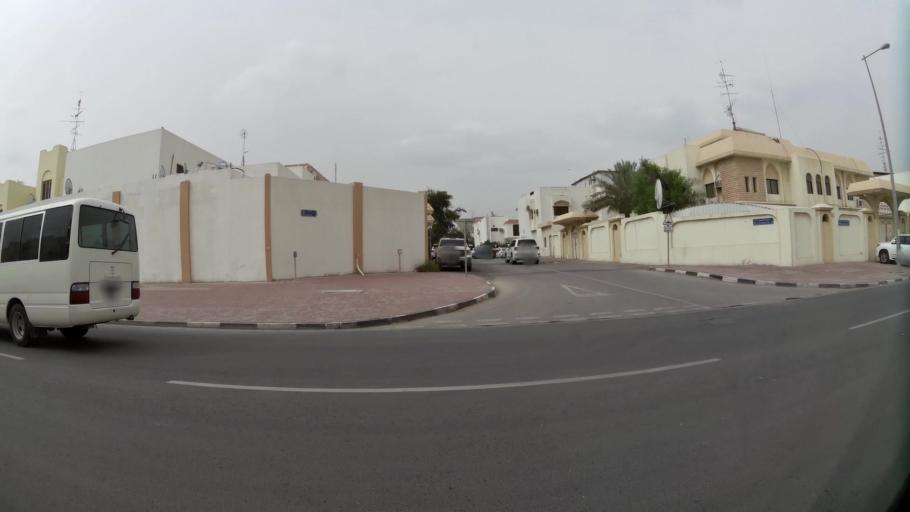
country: QA
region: Baladiyat ad Dawhah
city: Doha
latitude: 25.2516
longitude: 51.5211
